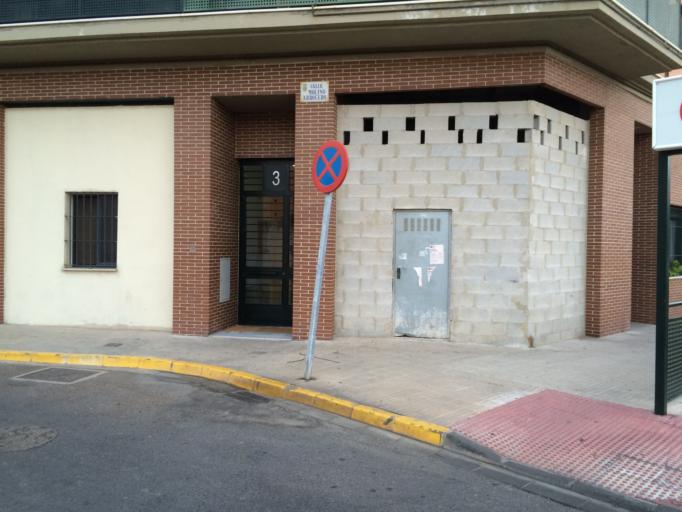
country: ES
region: Andalusia
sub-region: Provincia de Sevilla
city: Camas
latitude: 37.3968
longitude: -6.0336
